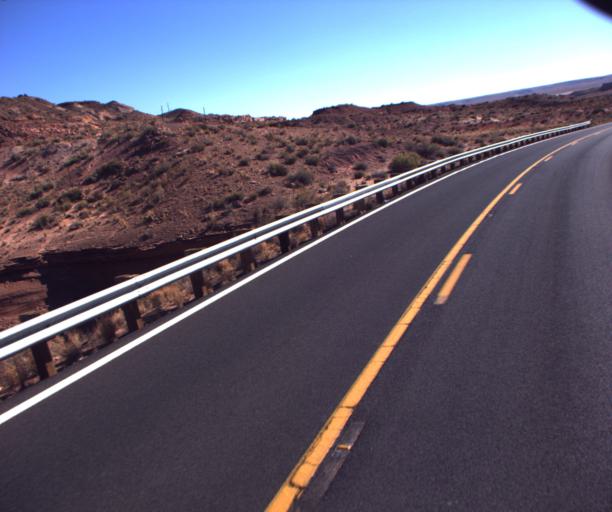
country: US
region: Arizona
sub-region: Coconino County
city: Tuba City
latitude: 36.1081
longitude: -111.2133
